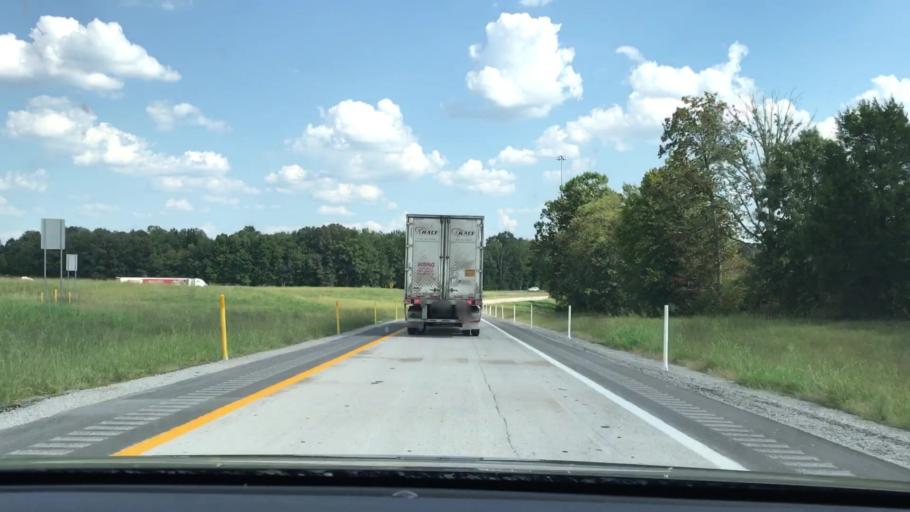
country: US
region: Kentucky
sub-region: Ohio County
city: Oak Grove
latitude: 37.3821
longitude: -86.8102
